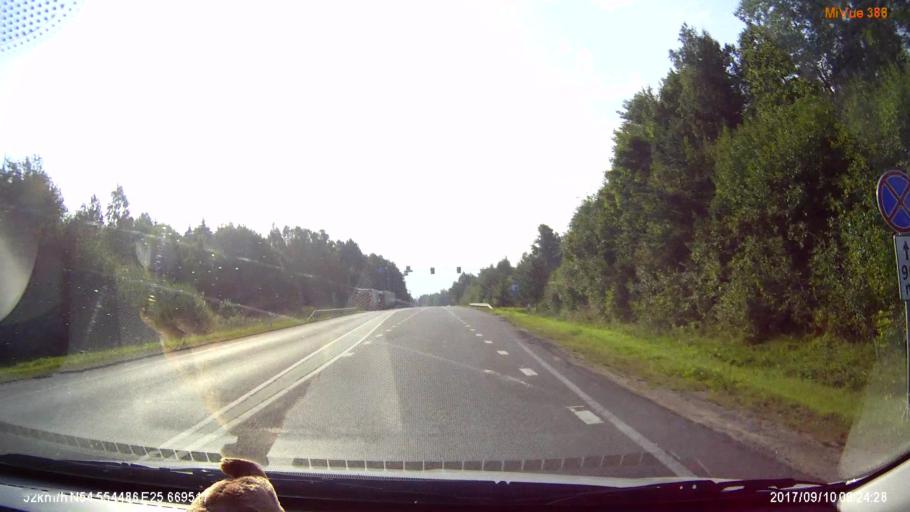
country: BY
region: Grodnenskaya
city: Astravyets
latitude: 54.5543
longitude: 25.6699
